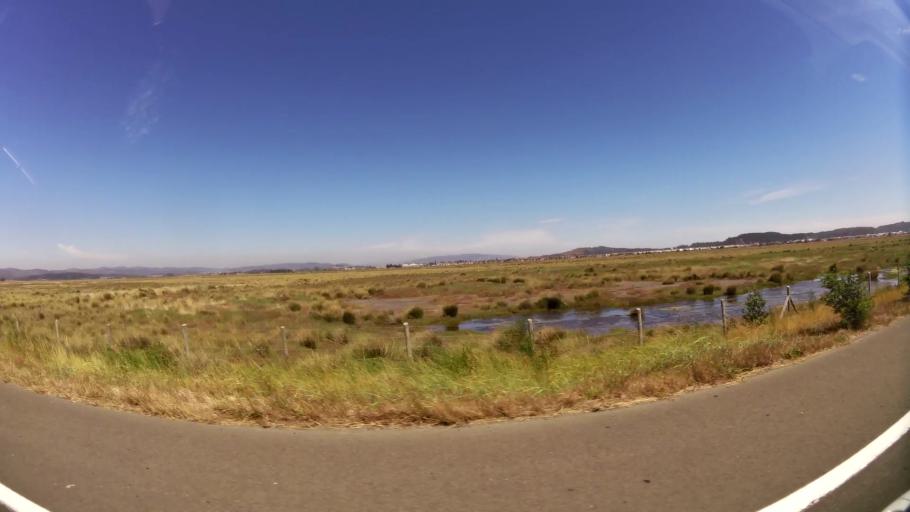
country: CL
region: Biobio
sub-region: Provincia de Concepcion
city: Talcahuano
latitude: -36.7340
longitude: -73.0784
